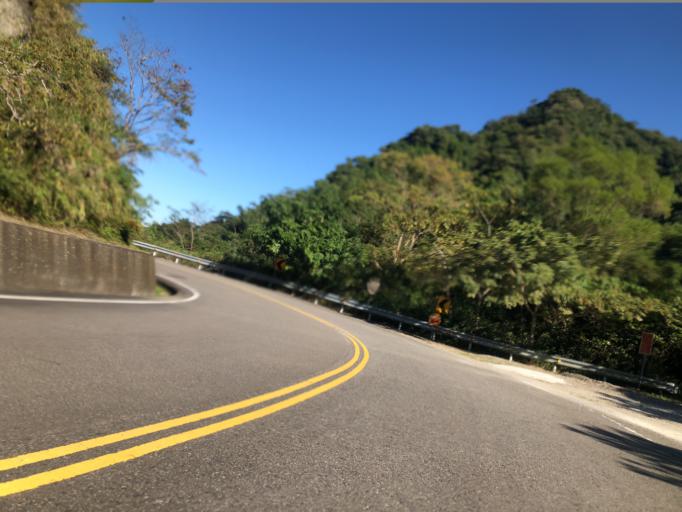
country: TW
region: Taiwan
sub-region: Miaoli
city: Miaoli
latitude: 24.5802
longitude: 120.9346
